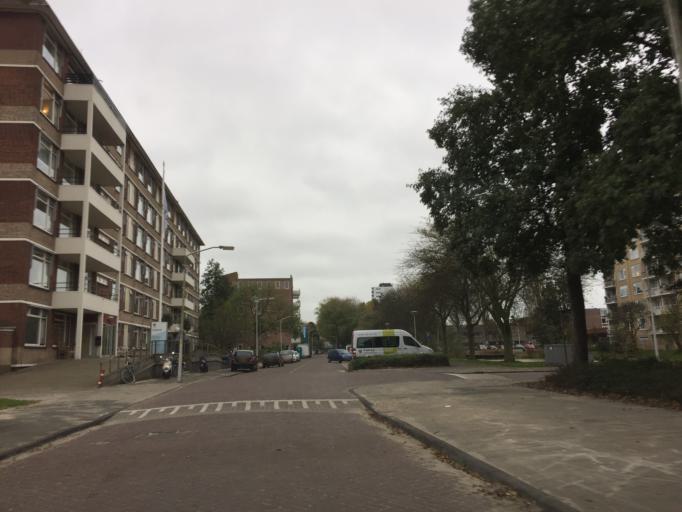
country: NL
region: South Holland
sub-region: Gemeente Leiden
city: Leiden
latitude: 52.1430
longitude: 4.4729
